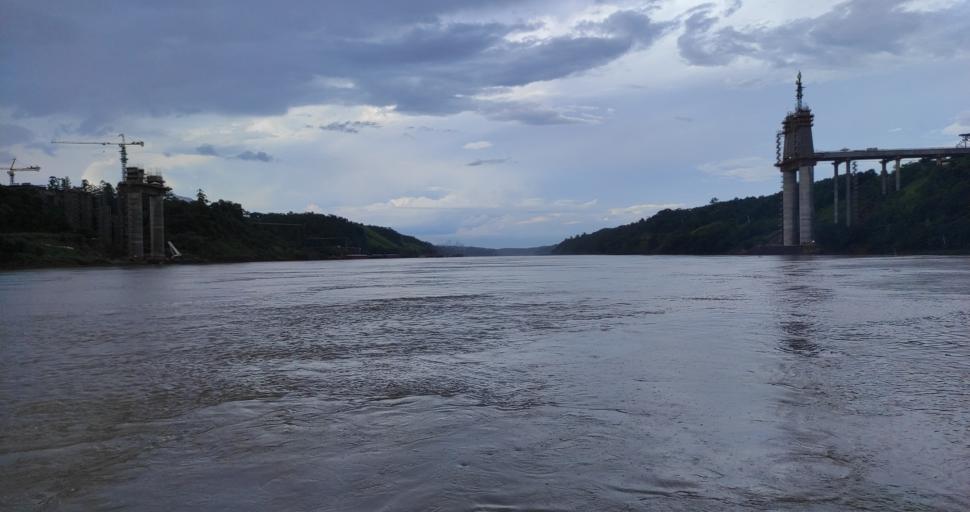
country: AR
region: Misiones
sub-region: Departamento de Iguazu
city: Puerto Iguazu
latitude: -25.5934
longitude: -54.5933
